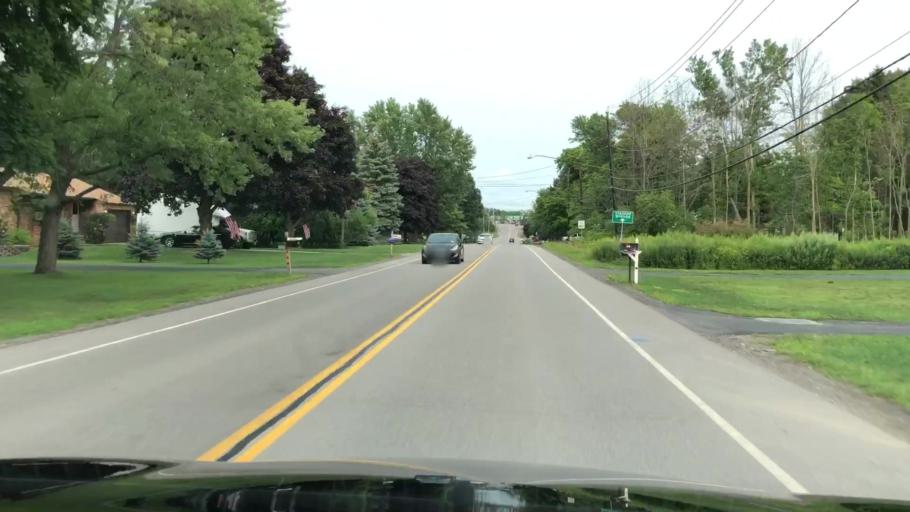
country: US
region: New York
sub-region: Erie County
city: Orchard Park
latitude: 42.7964
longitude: -78.7595
